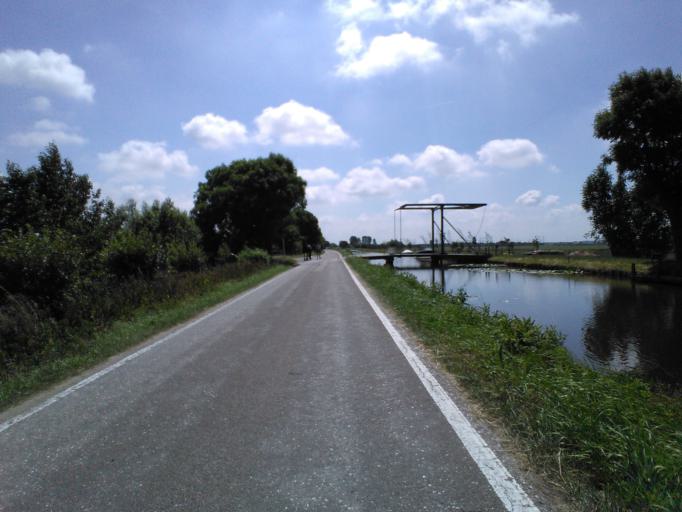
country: NL
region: South Holland
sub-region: Gemeente Maassluis
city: Maassluis
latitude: 51.9482
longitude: 4.2944
